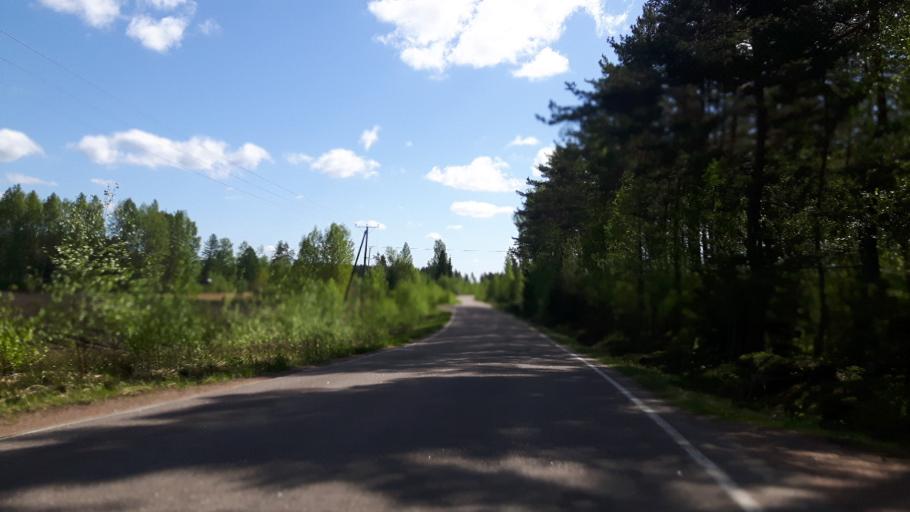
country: FI
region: Kymenlaakso
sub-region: Kotka-Hamina
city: Hamina
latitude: 60.5260
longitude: 27.3009
